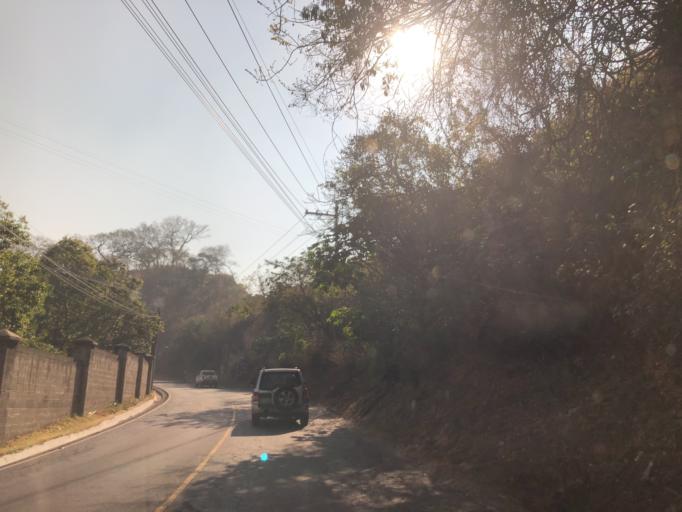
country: GT
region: Guatemala
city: Petapa
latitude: 14.5035
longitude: -90.5416
